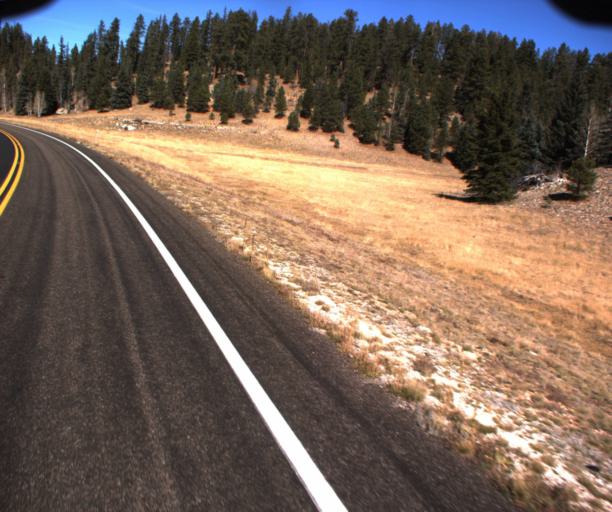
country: US
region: Arizona
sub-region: Coconino County
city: Grand Canyon
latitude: 36.5392
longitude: -112.1578
